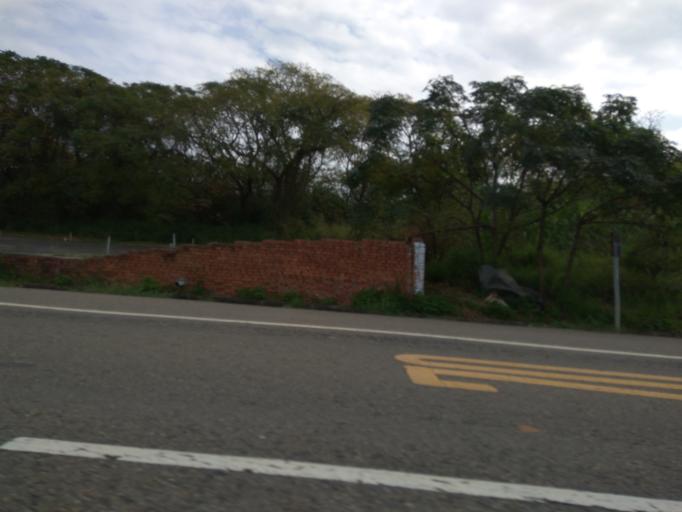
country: TW
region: Taiwan
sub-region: Hsinchu
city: Zhubei
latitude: 24.9550
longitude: 121.0120
